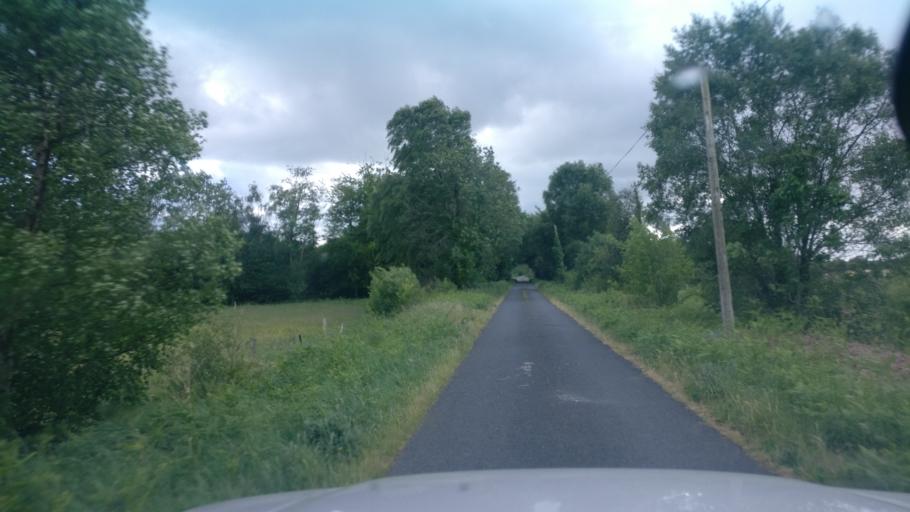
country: IE
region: Connaught
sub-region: County Galway
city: Portumna
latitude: 53.1863
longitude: -8.3299
